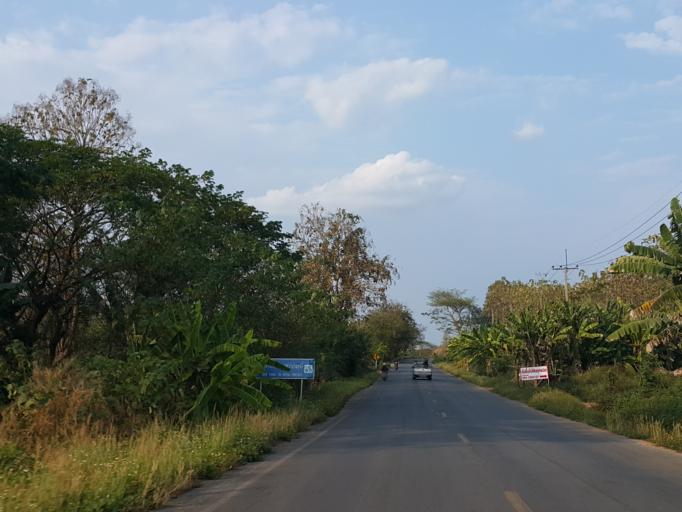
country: TH
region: Lampang
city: Hang Chat
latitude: 18.4450
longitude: 99.4512
